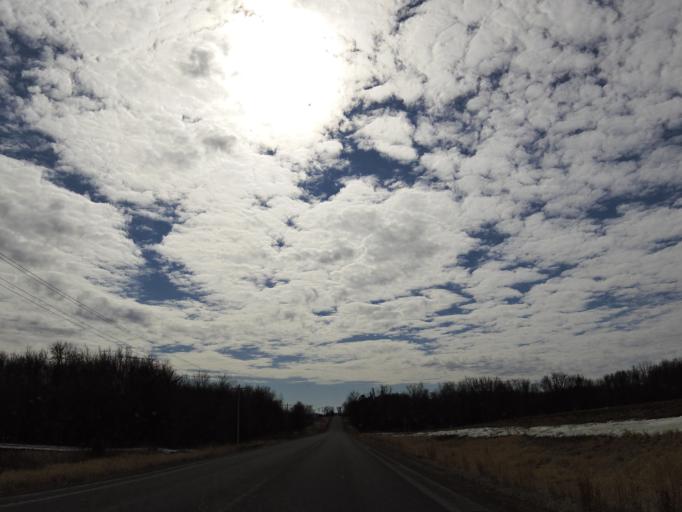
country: US
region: Minnesota
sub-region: Le Sueur County
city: New Prague
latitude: 44.5687
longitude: -93.5573
